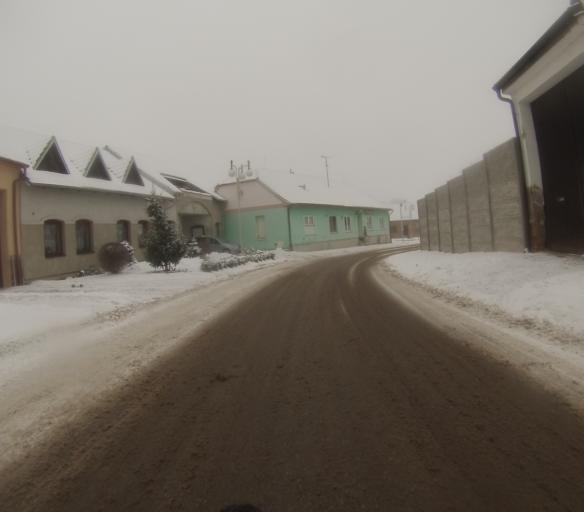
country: CZ
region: South Moravian
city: Strelice
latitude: 49.1521
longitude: 16.5033
